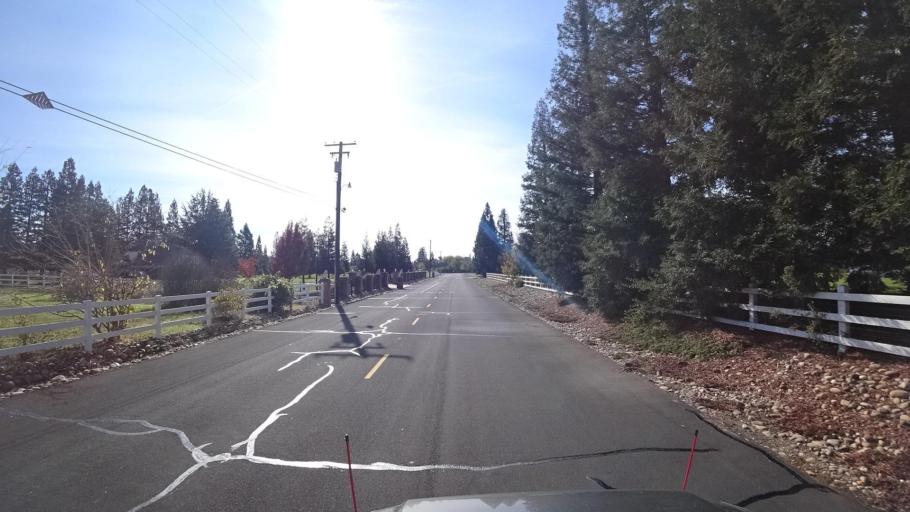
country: US
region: California
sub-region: Sacramento County
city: Wilton
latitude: 38.4296
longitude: -121.2845
